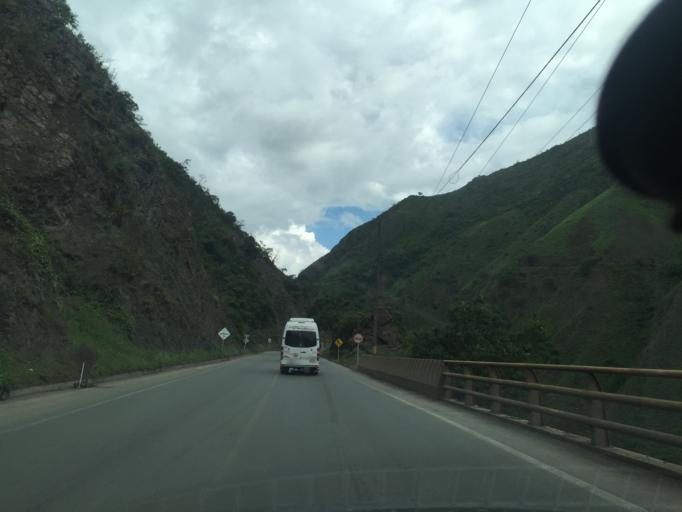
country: CO
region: Valle del Cauca
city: Dagua
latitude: 3.7744
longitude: -76.6982
